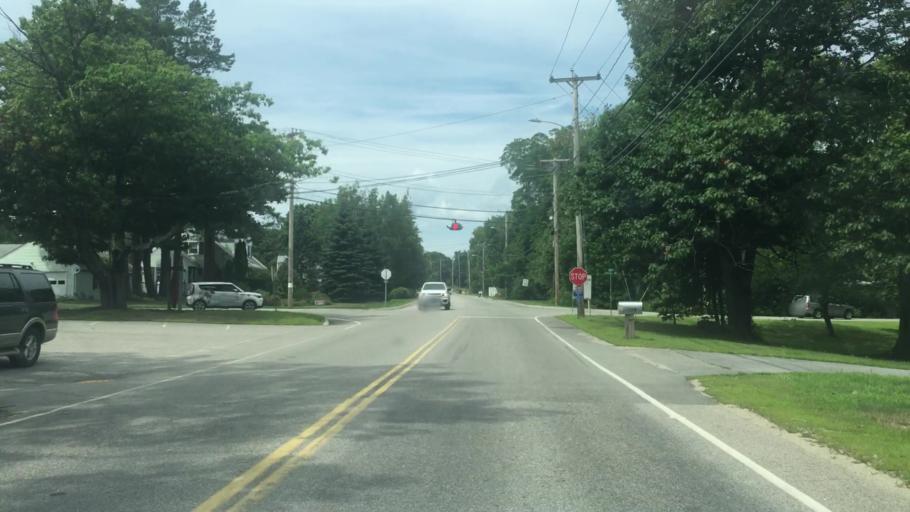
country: US
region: Maine
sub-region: Cumberland County
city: Scarborough
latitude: 43.5904
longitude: -70.2957
